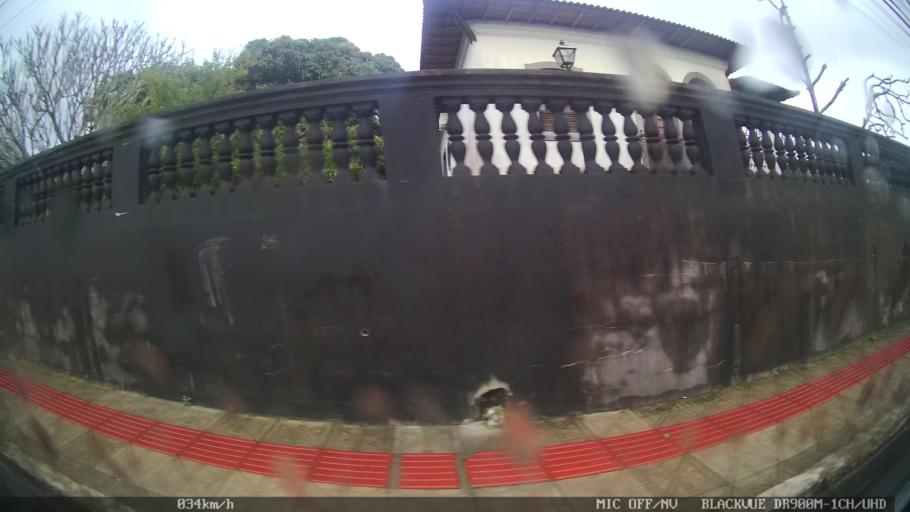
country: BR
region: Santa Catarina
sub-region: Sao Jose
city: Campinas
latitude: -27.6096
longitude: -48.6283
